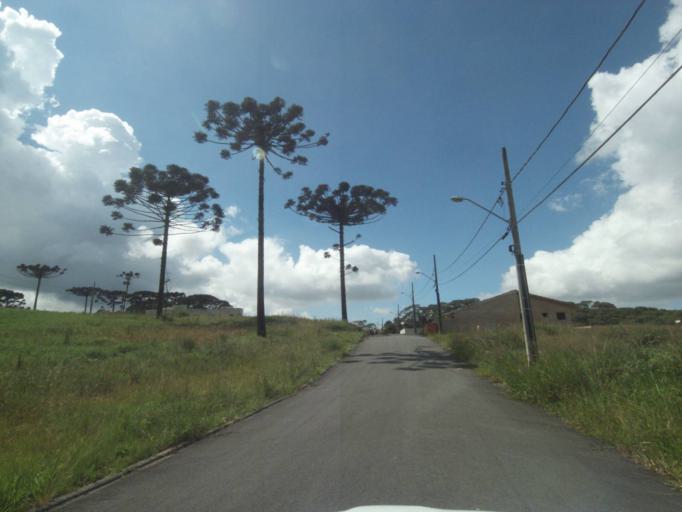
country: BR
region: Parana
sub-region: Colombo
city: Colombo
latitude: -25.3129
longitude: -49.2331
